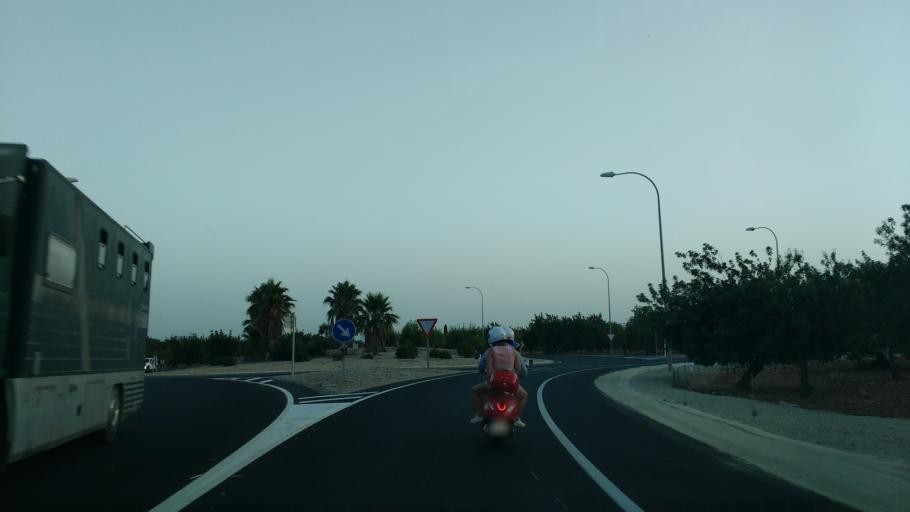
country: ES
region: Balearic Islands
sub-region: Illes Balears
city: Bunyola
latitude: 39.6688
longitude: 2.6768
